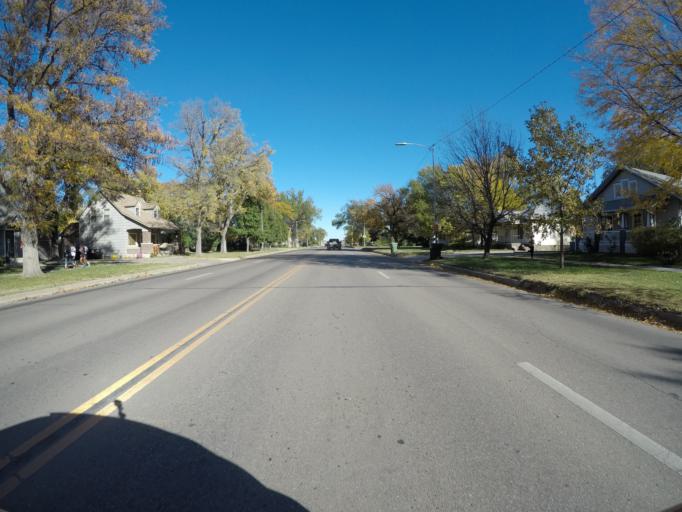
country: US
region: Kansas
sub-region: Thomas County
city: Colby
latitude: 39.3971
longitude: -101.0528
